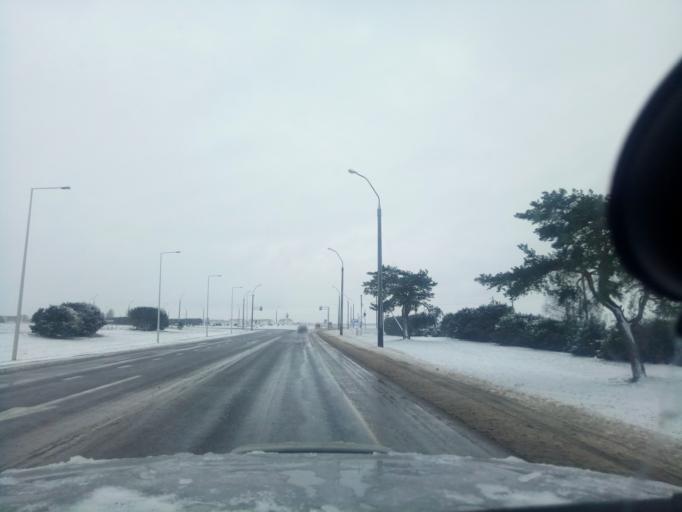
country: BY
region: Minsk
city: Nyasvizh
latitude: 53.2402
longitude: 26.6319
